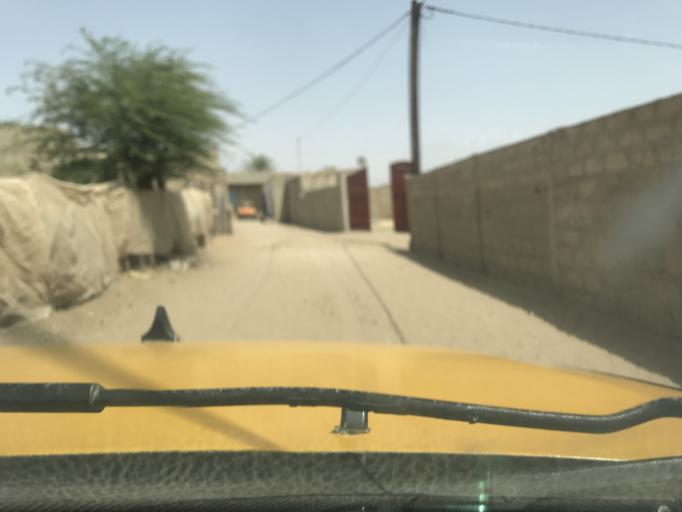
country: SN
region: Saint-Louis
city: Saint-Louis
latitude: 16.0177
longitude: -16.4463
